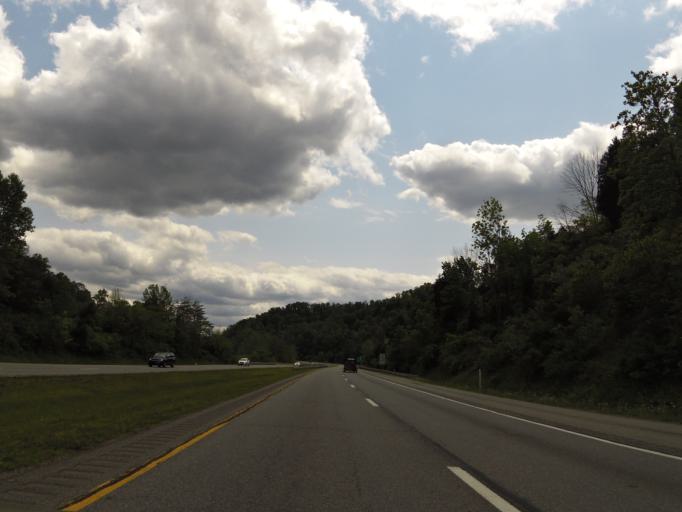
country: US
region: West Virginia
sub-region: Kanawha County
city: Sissonville
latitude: 38.5641
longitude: -81.6363
